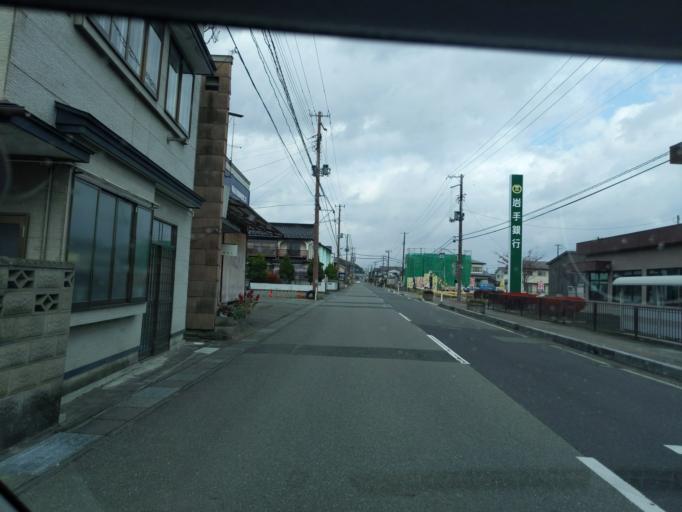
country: JP
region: Iwate
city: Mizusawa
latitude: 39.0529
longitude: 141.1240
